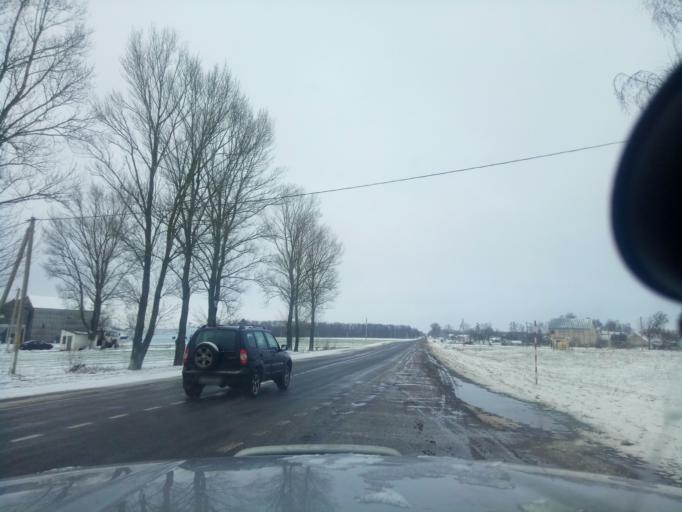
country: BY
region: Minsk
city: Tsimkavichy
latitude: 53.0773
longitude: 27.0013
